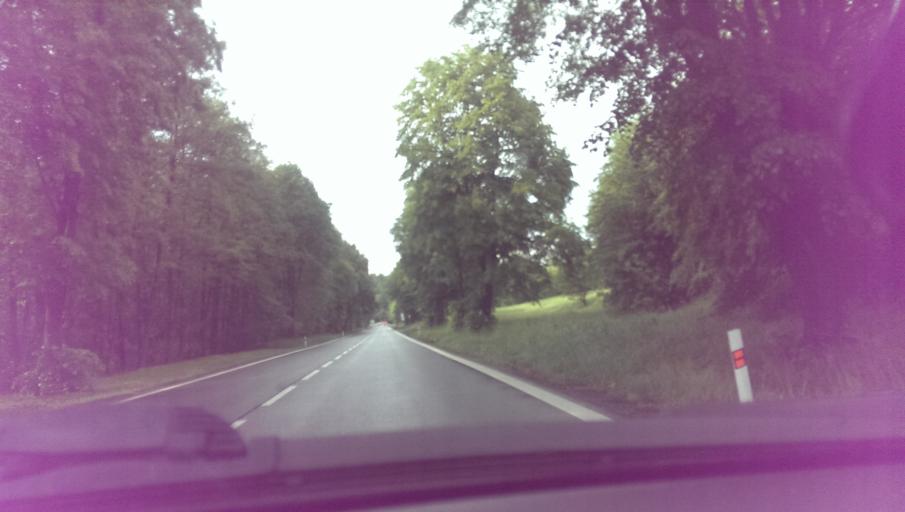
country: CZ
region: Zlin
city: Breznice
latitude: 49.1728
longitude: 17.6403
